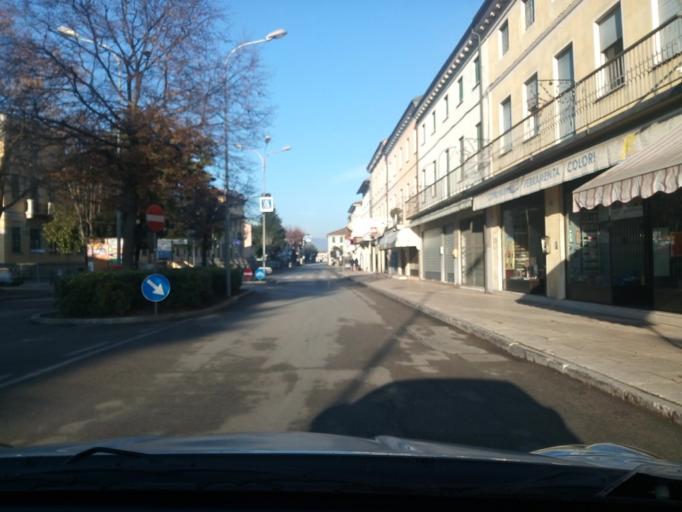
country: IT
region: Veneto
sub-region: Provincia di Vicenza
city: Dueville
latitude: 45.6363
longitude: 11.5491
